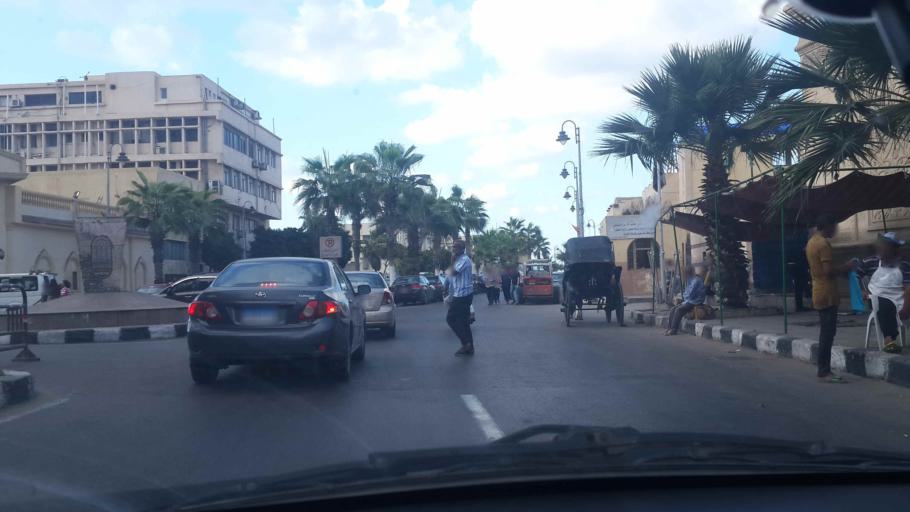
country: EG
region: Alexandria
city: Alexandria
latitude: 31.2097
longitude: 29.8822
